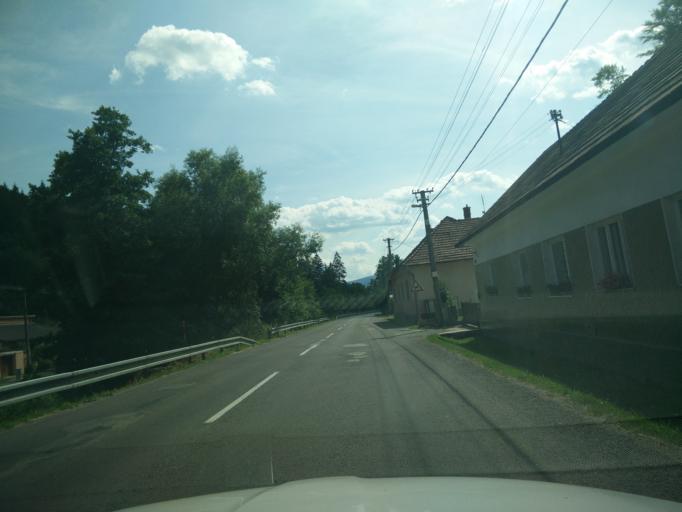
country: SK
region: Nitriansky
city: Prievidza
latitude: 48.8996
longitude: 18.6479
